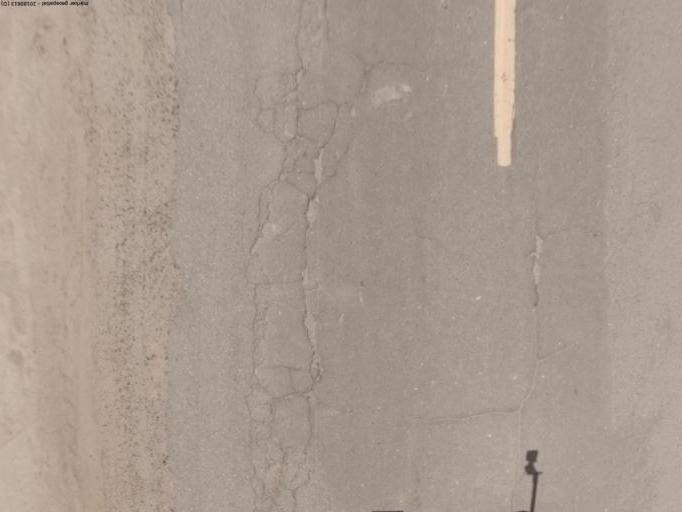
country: US
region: California
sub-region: Madera County
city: Chowchilla
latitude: 37.0738
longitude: -120.3650
